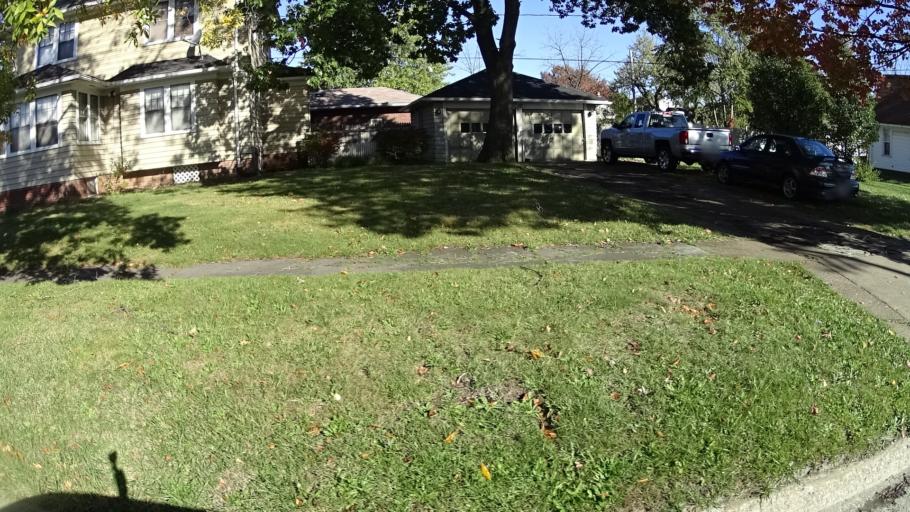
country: US
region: Ohio
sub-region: Lorain County
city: Lorain
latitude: 41.4388
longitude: -82.1634
